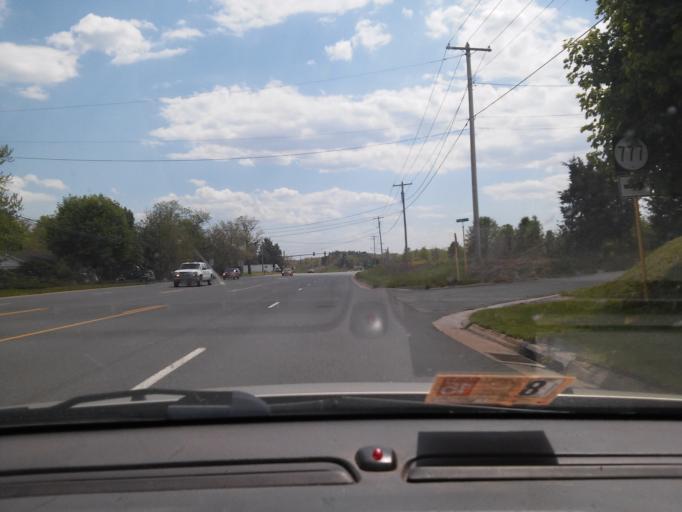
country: US
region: Virginia
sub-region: City of Winchester
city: Winchester
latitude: 39.1469
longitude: -78.1605
